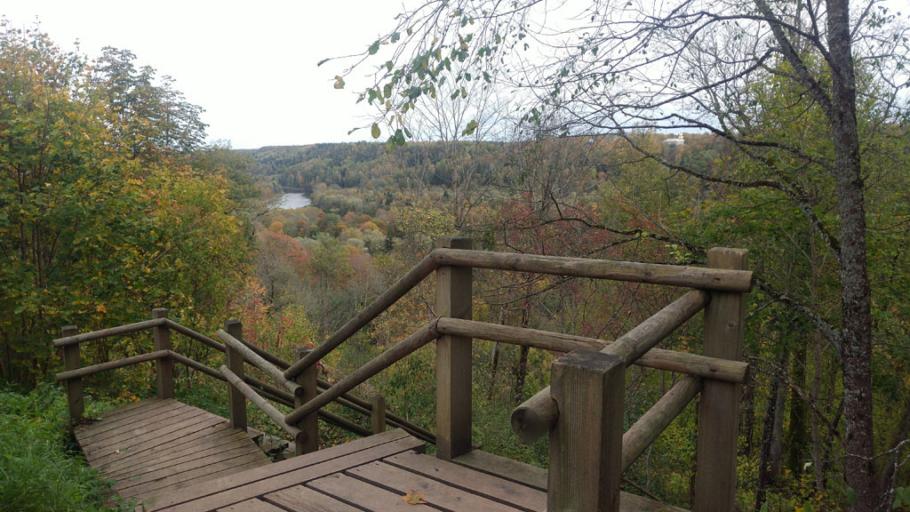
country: LV
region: Sigulda
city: Sigulda
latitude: 57.1674
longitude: 24.8298
